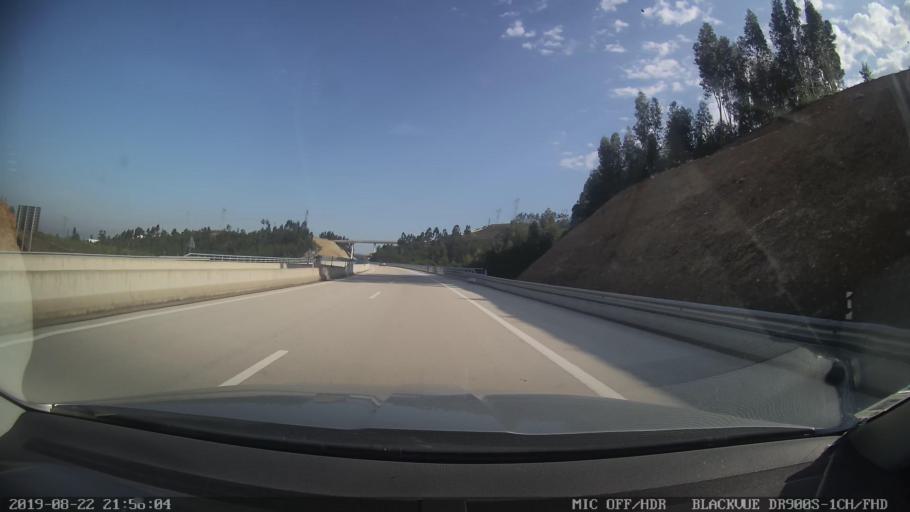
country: PT
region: Coimbra
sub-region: Coimbra
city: Coimbra
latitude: 40.1641
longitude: -8.3783
